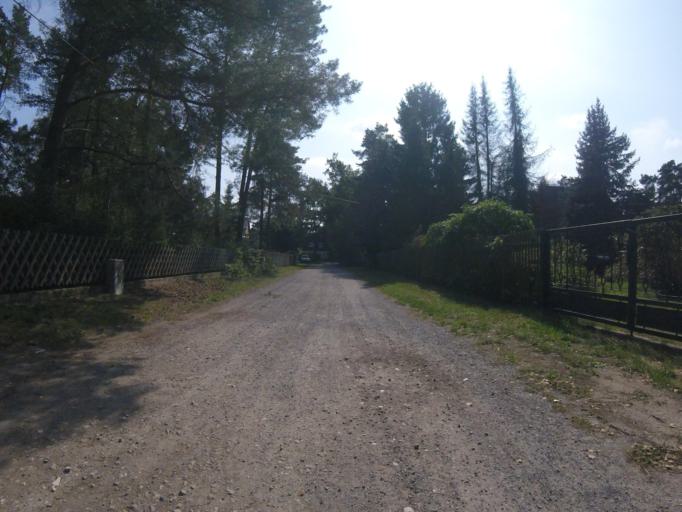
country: DE
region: Brandenburg
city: Bestensee
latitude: 52.2732
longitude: 13.7448
